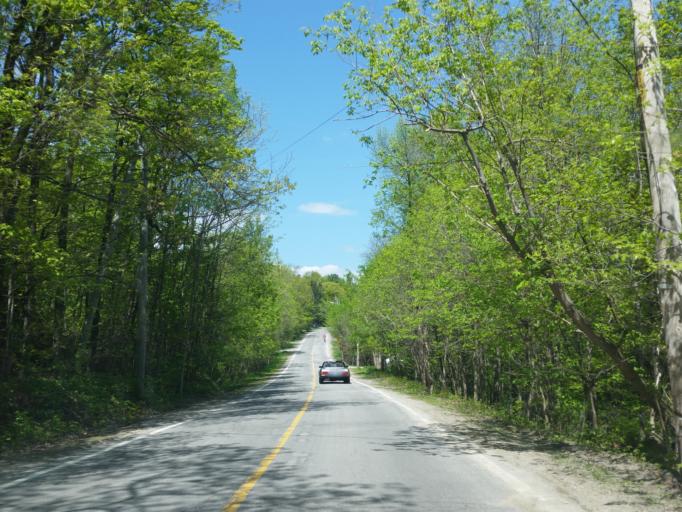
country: CA
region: Quebec
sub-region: Outaouais
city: Wakefield
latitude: 45.5904
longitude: -75.8718
